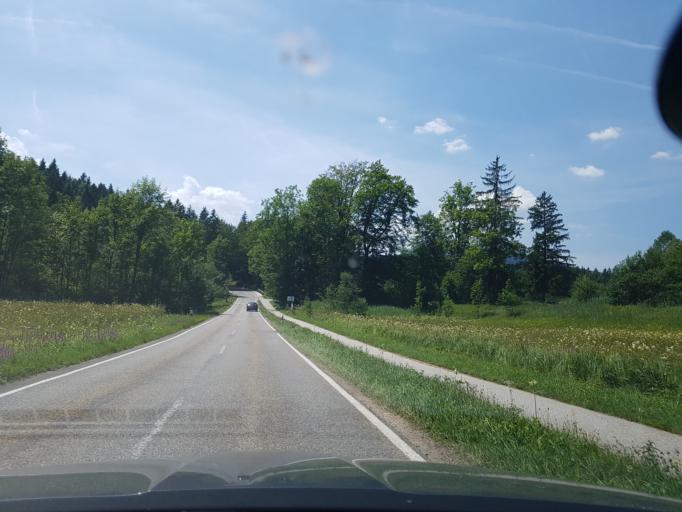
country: DE
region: Bavaria
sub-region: Upper Bavaria
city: Berchtesgaden
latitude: 47.6447
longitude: 12.9878
